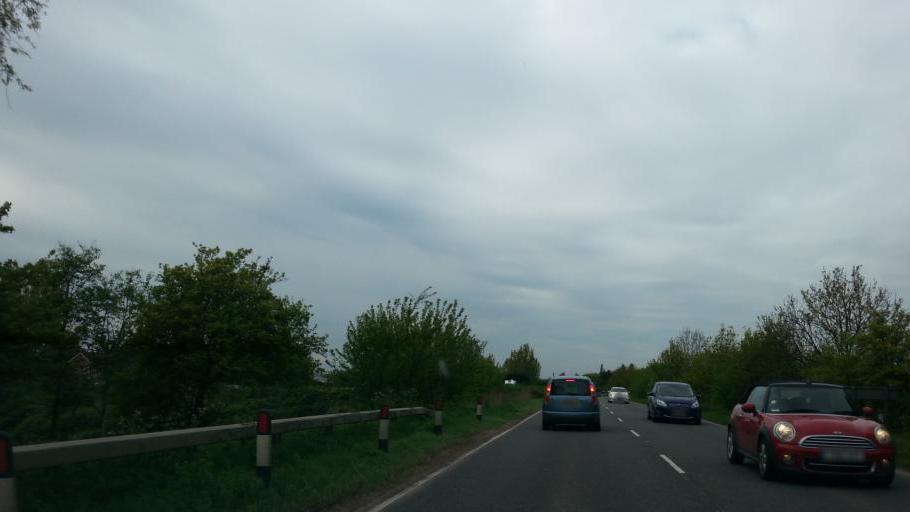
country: GB
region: England
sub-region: Cambridgeshire
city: March
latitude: 52.5535
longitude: 0.0678
